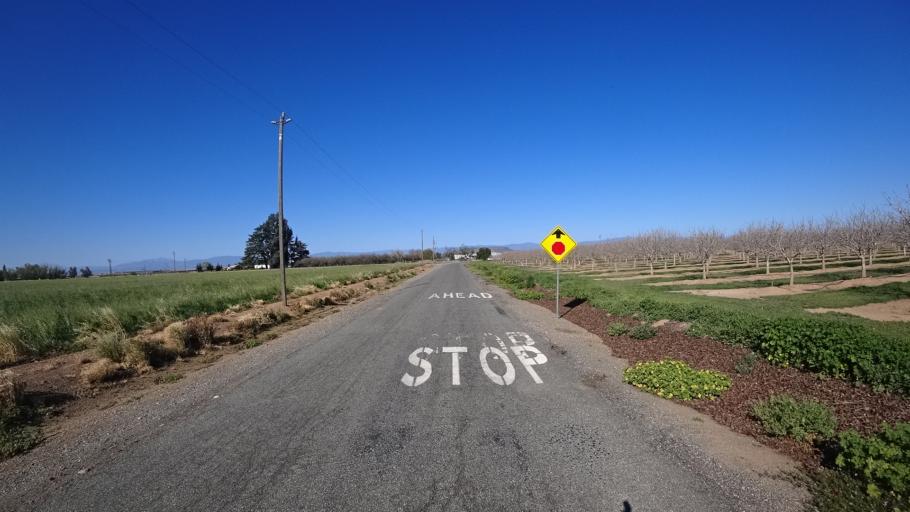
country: US
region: California
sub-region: Glenn County
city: Orland
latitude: 39.7443
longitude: -122.2462
